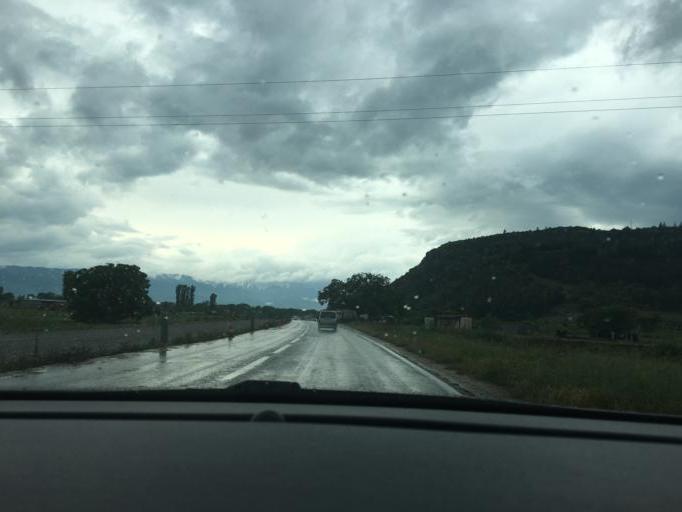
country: MK
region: Ohrid
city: Ohrid
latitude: 41.1365
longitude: 20.7713
